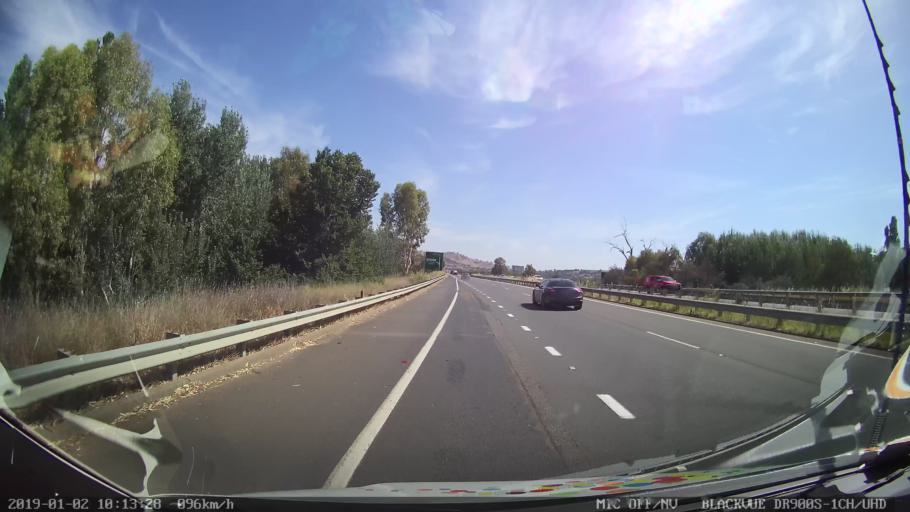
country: AU
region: New South Wales
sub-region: Gundagai
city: Gundagai
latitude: -35.0796
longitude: 148.0937
